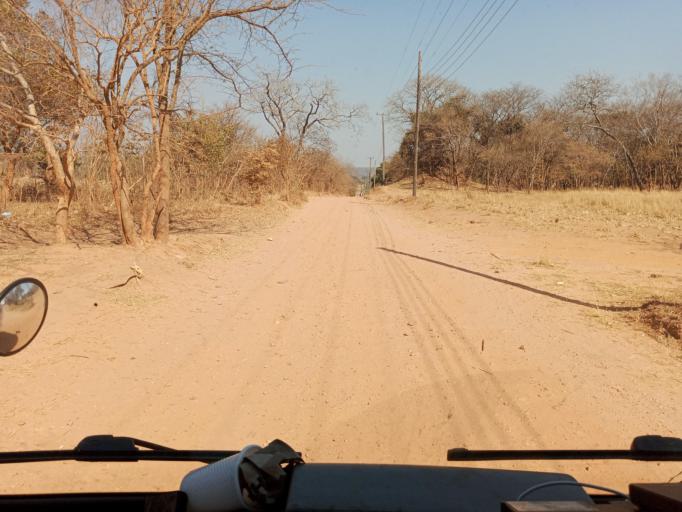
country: ZM
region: Lusaka
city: Lusaka
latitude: -15.3384
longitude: 28.1985
